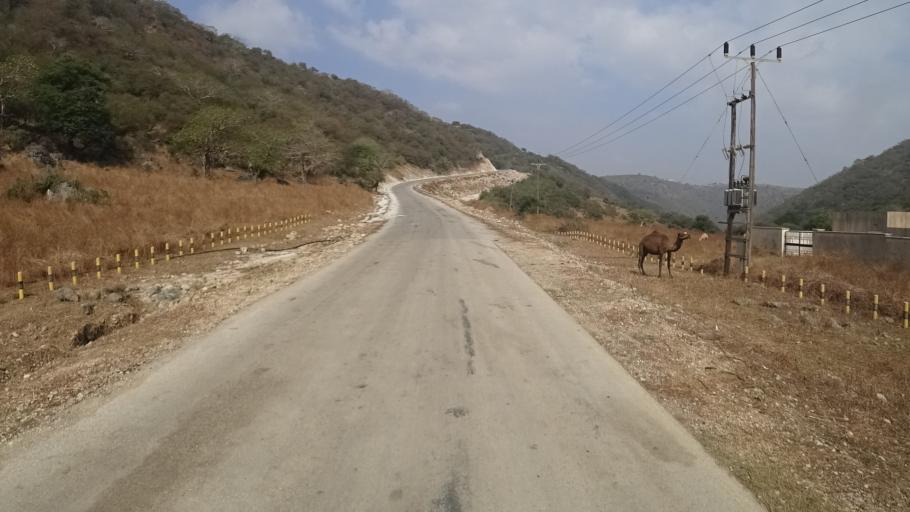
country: YE
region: Al Mahrah
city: Hawf
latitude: 16.7209
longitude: 53.2699
